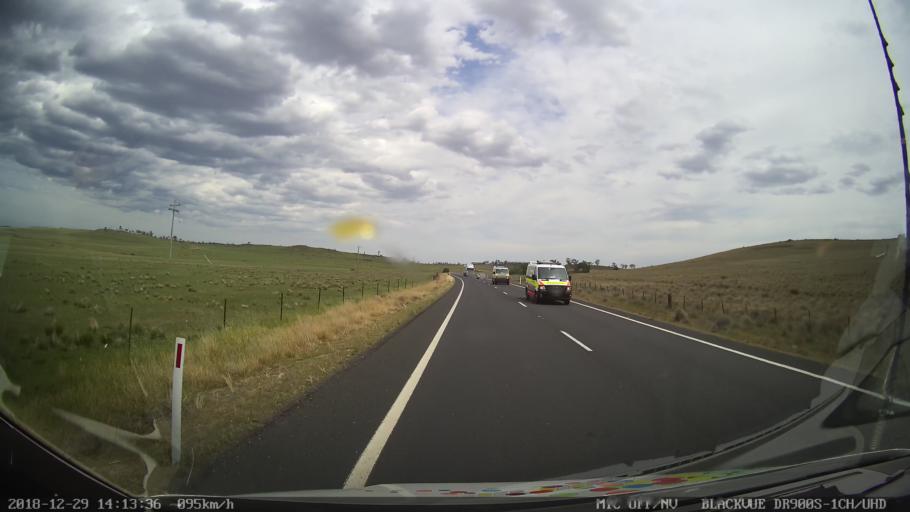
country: AU
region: New South Wales
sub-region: Cooma-Monaro
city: Cooma
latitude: -36.4305
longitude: 149.2384
